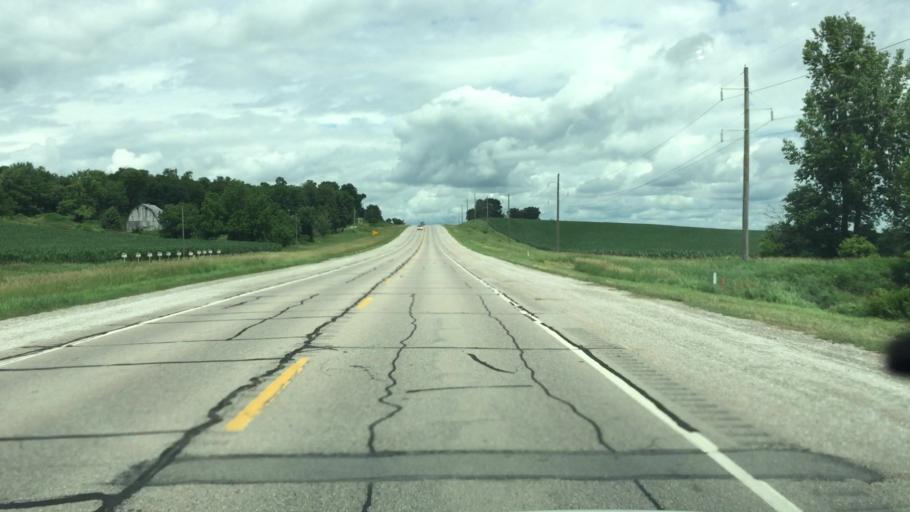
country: US
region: Iowa
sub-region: Jasper County
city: Monroe
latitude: 41.5872
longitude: -93.0970
